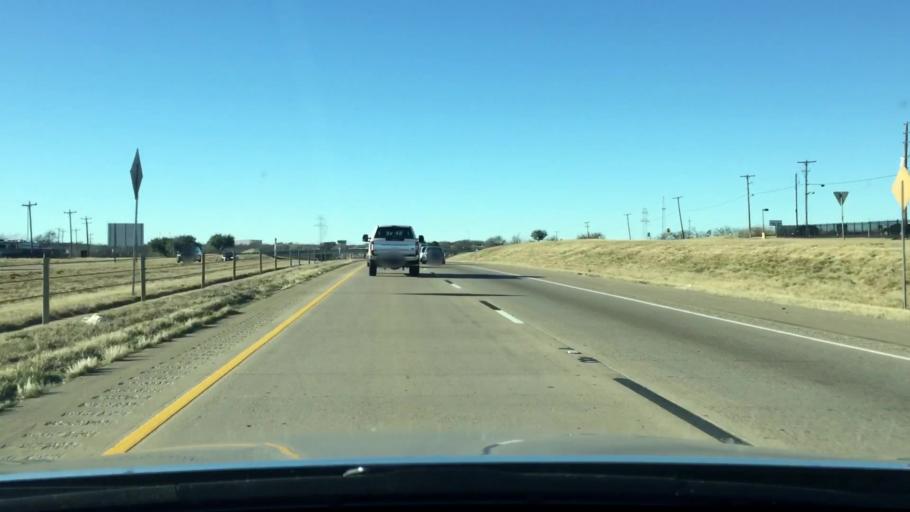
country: US
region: Texas
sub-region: Johnson County
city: Alvarado
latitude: 32.4277
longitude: -97.2356
